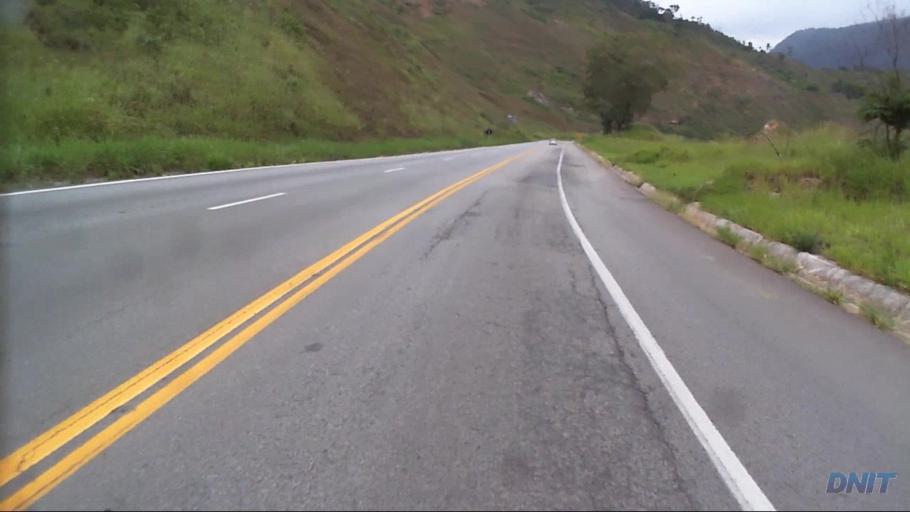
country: BR
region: Minas Gerais
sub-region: Nova Era
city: Nova Era
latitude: -19.6461
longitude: -42.9058
